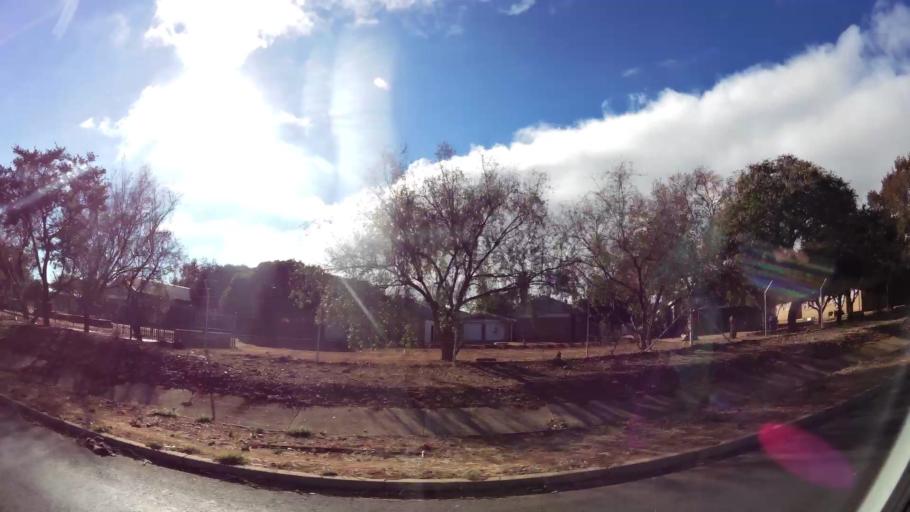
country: ZA
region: Limpopo
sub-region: Capricorn District Municipality
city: Polokwane
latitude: -23.9175
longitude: 29.4762
